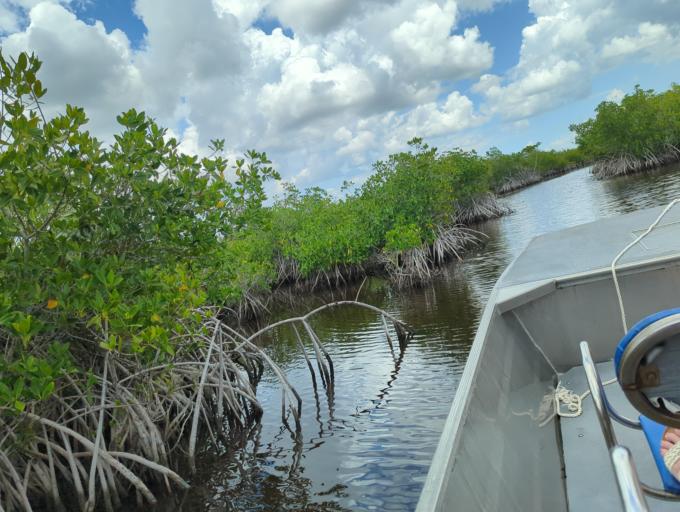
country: US
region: Florida
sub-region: Collier County
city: Marco
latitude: 25.9069
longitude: -81.3726
